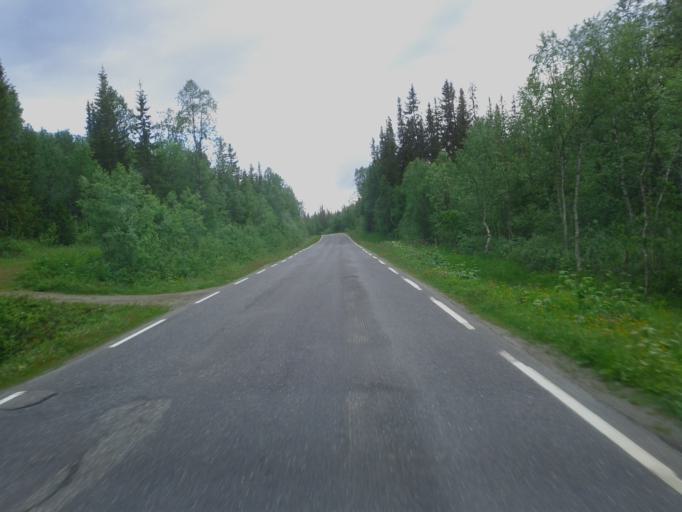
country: NO
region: Nordland
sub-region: Hattfjelldal
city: Hattfjelldal
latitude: 65.5669
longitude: 13.7682
